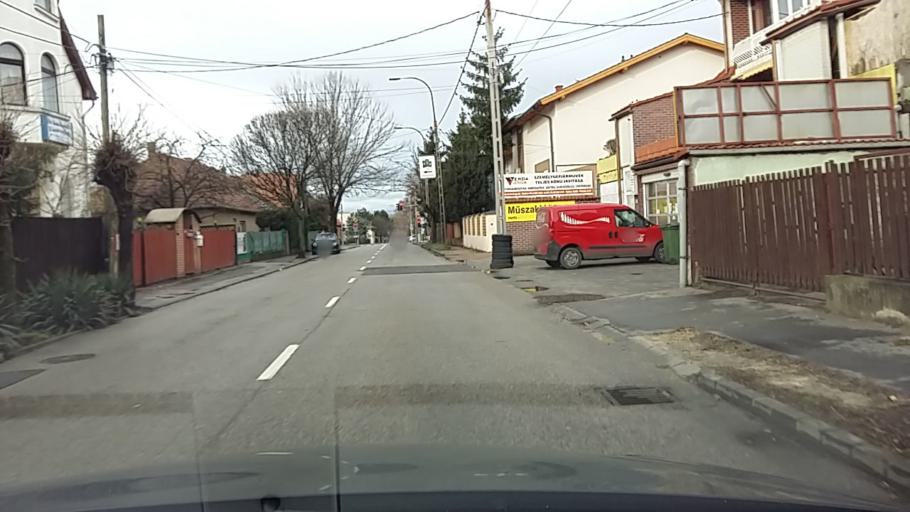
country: HU
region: Budapest
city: Budapest XVI. keruelet
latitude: 47.5253
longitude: 19.1631
